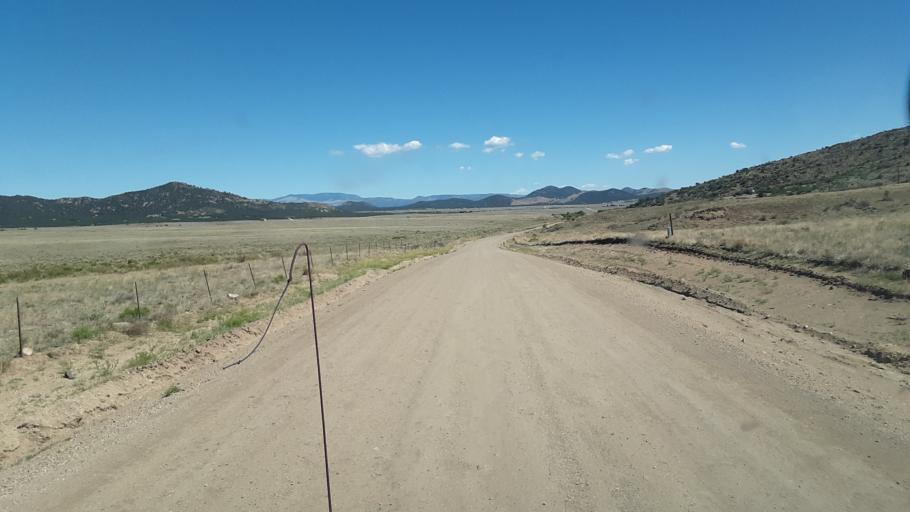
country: US
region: Colorado
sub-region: Custer County
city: Westcliffe
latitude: 38.2342
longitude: -105.5022
